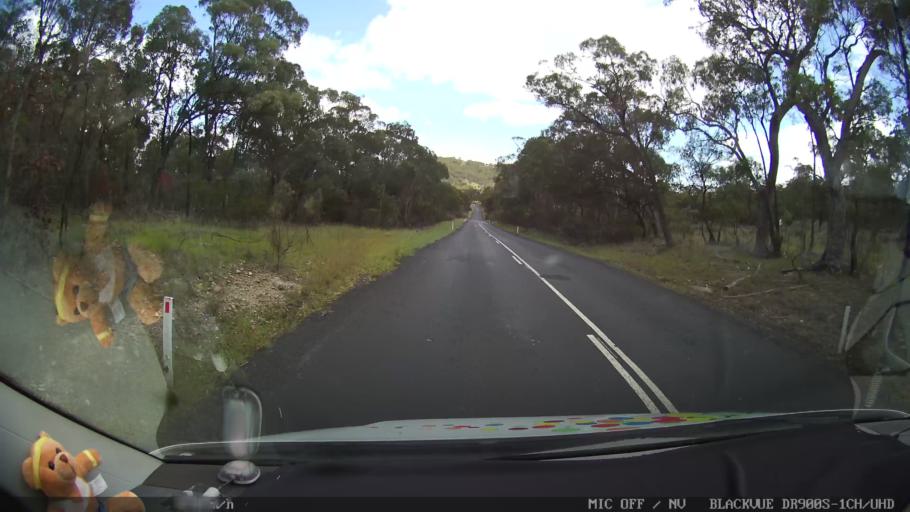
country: AU
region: New South Wales
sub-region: Glen Innes Severn
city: Glen Innes
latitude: -29.5420
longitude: 151.6697
